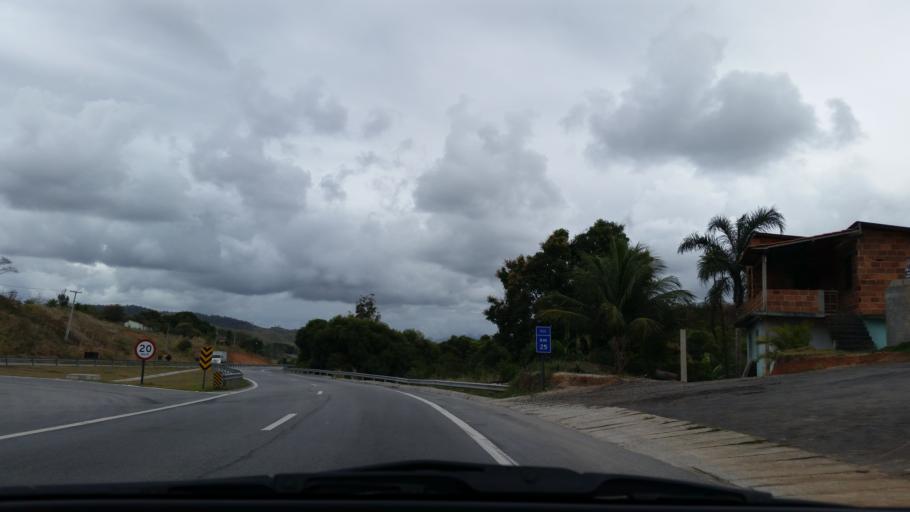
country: BR
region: Rio de Janeiro
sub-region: Araruama
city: Araruama
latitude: -22.7980
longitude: -42.4340
